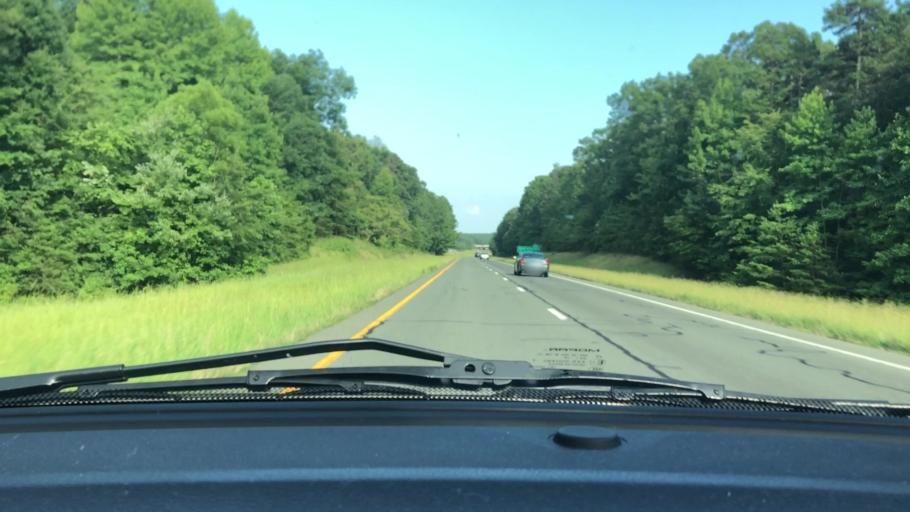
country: US
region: North Carolina
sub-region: Chatham County
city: Siler City
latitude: 35.7713
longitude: -79.4888
